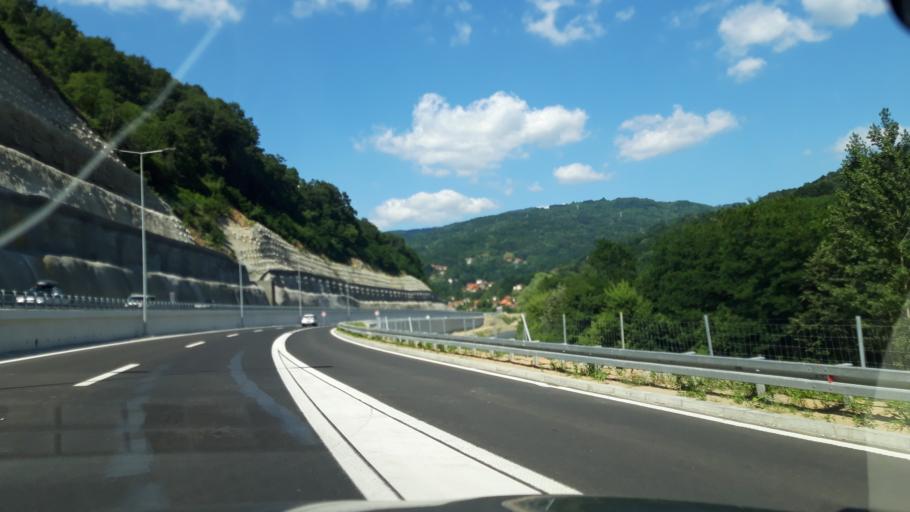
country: RS
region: Central Serbia
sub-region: Pcinjski Okrug
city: Vladicin Han
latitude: 42.8220
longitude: 22.1222
